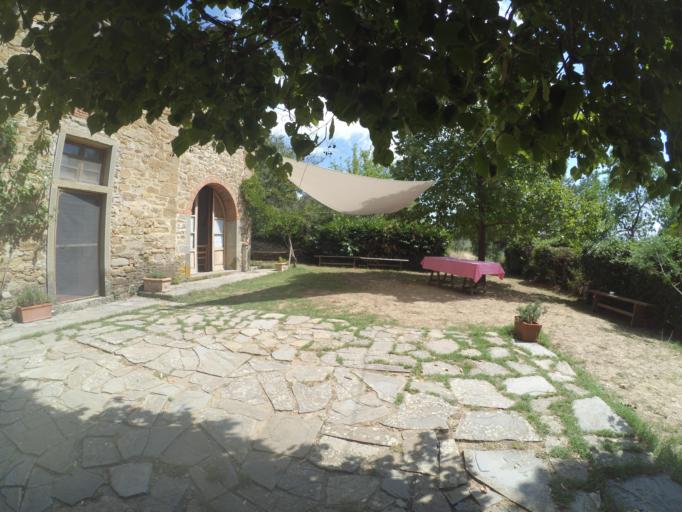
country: IT
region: Tuscany
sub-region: Province of Arezzo
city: Castiglion Fibocchi
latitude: 43.5292
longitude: 11.7806
